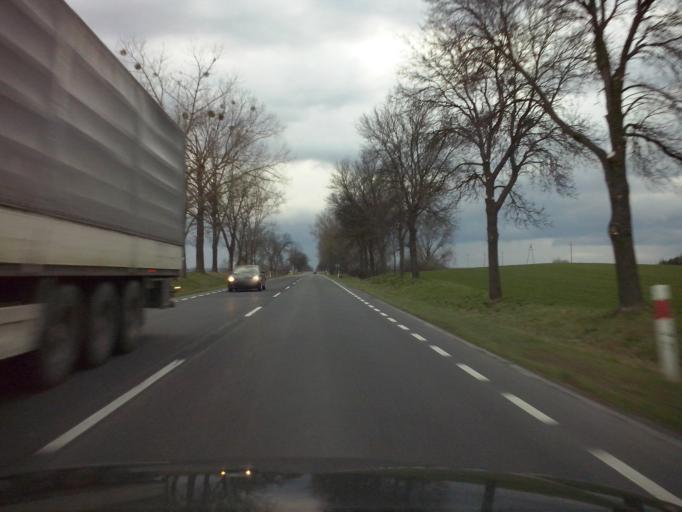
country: PL
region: Lublin Voivodeship
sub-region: Powiat chelmski
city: Rejowiec
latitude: 51.1697
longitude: 23.3263
